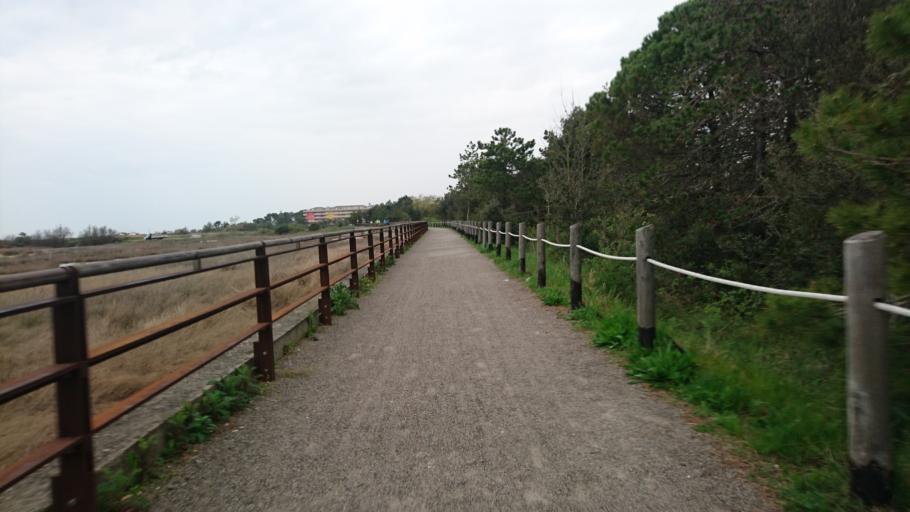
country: IT
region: Veneto
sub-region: Provincia di Venezia
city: Bibione
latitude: 45.6357
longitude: 13.0784
